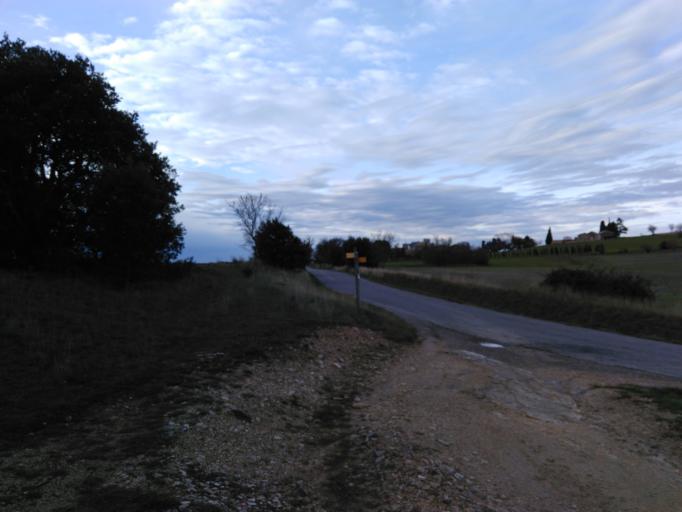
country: FR
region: Provence-Alpes-Cote d'Azur
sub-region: Departement du Vaucluse
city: Gordes
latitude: 43.9556
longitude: 5.2476
